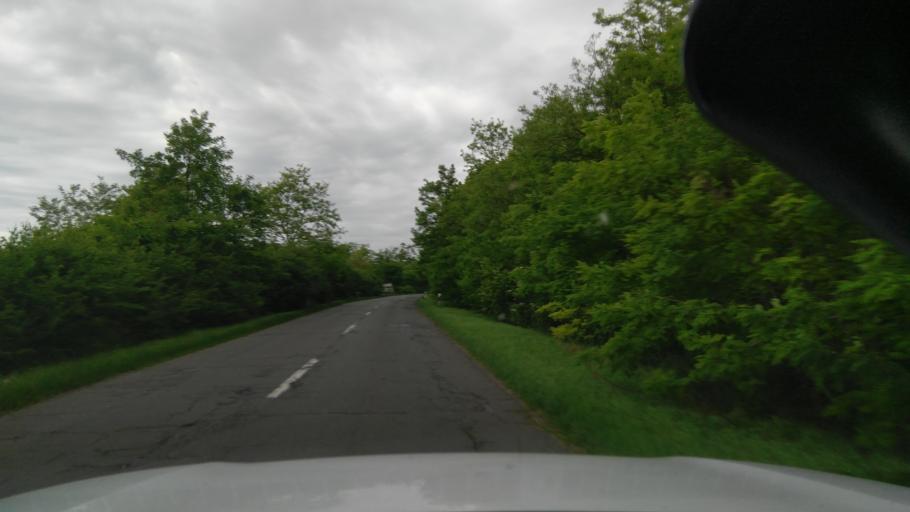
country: HU
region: Bekes
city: Bekescsaba
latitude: 46.6806
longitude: 21.1674
